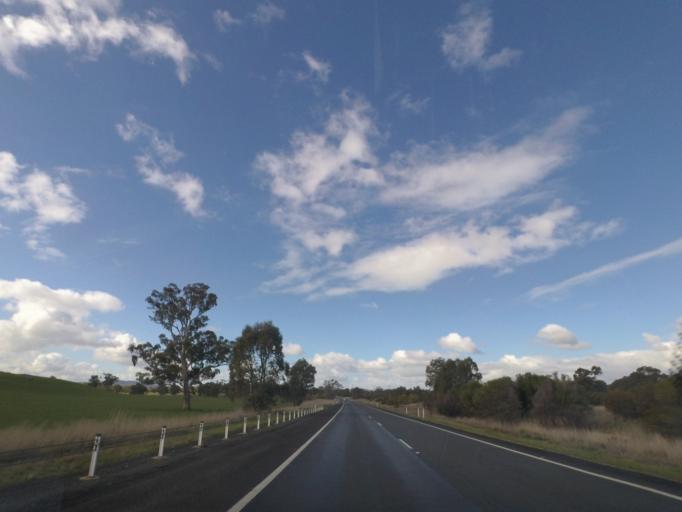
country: AU
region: New South Wales
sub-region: Greater Hume Shire
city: Jindera
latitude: -35.9248
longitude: 147.0271
